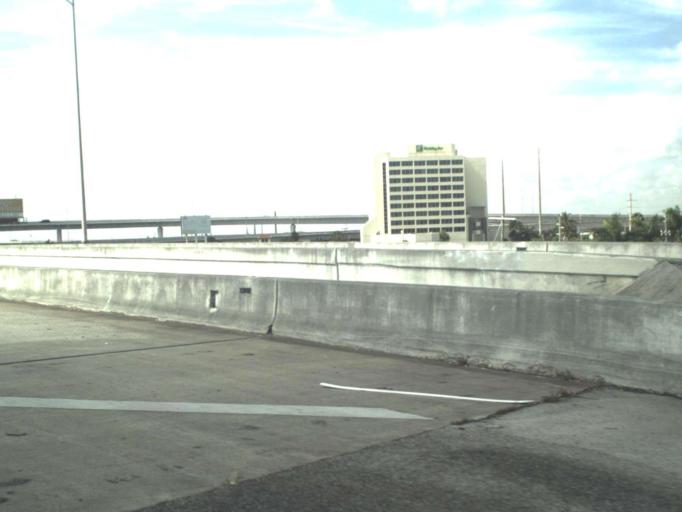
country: US
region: Florida
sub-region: Palm Beach County
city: West Palm Beach
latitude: 26.6941
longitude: -80.0685
